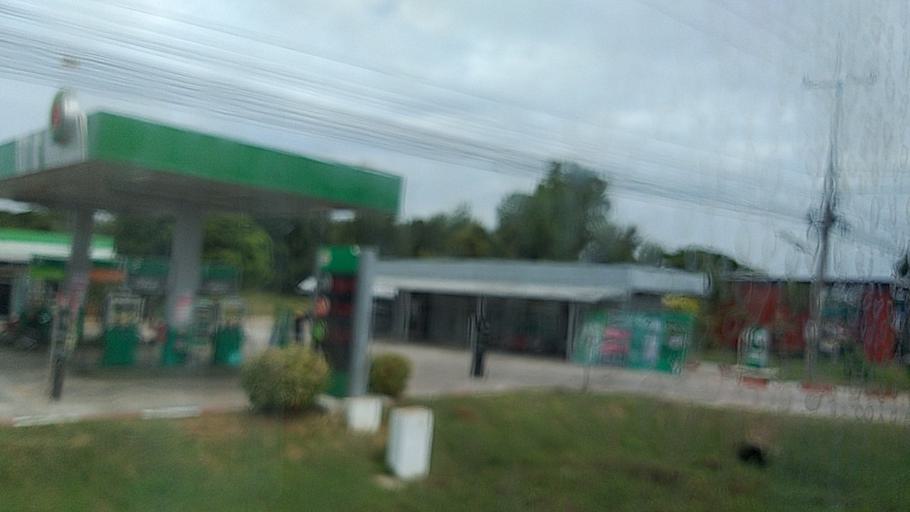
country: TH
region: Roi Et
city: Changhan
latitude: 16.1019
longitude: 103.5249
